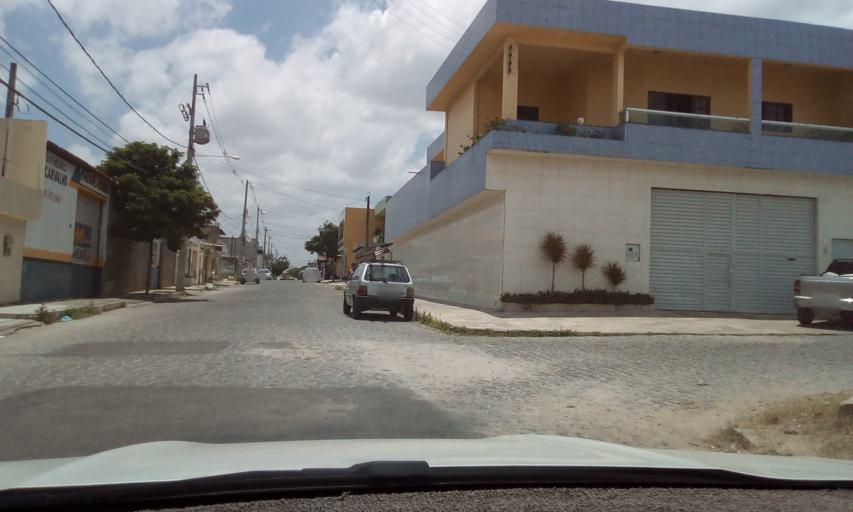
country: BR
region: Pernambuco
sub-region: Caruaru
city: Caruaru
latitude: -8.2692
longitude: -35.9871
